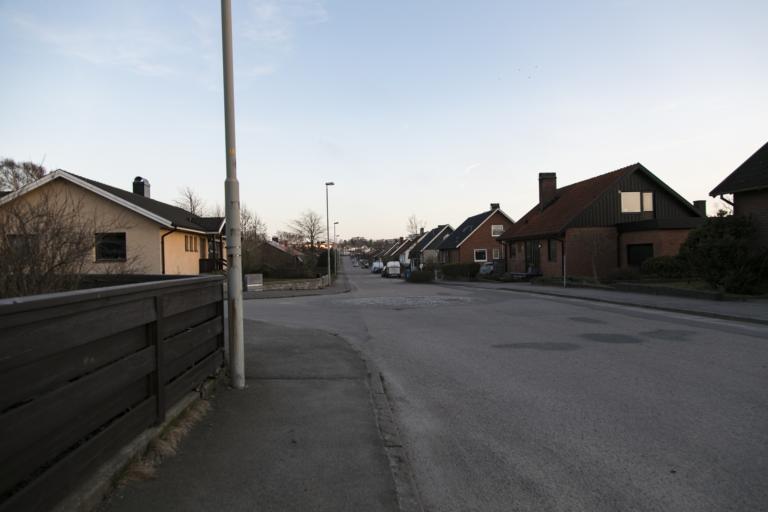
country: SE
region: Halland
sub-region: Varbergs Kommun
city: Varberg
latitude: 57.0987
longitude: 12.2586
